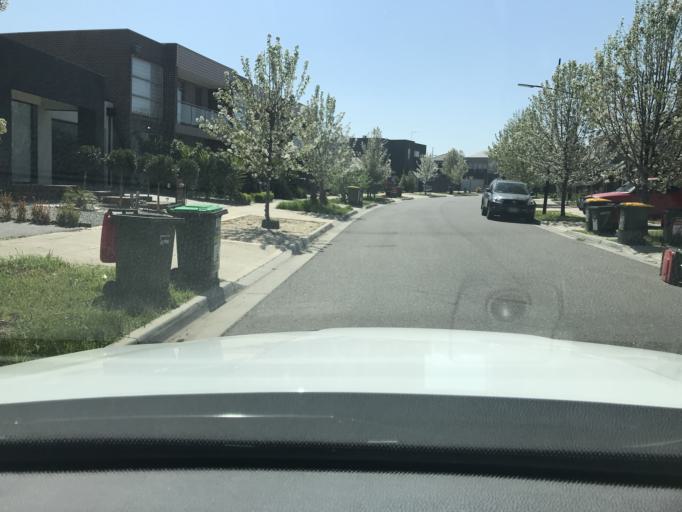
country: AU
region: Victoria
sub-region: Hume
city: Craigieburn
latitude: -37.5897
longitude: 144.9165
